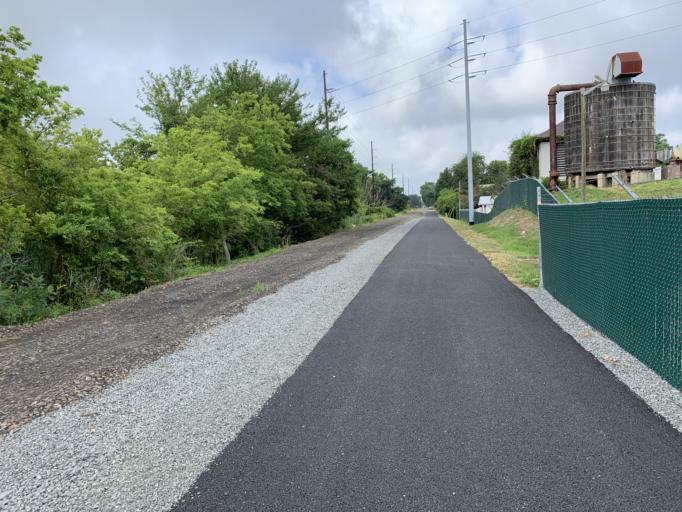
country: US
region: Delaware
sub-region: Sussex County
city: Lewes
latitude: 38.7708
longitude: -75.1373
